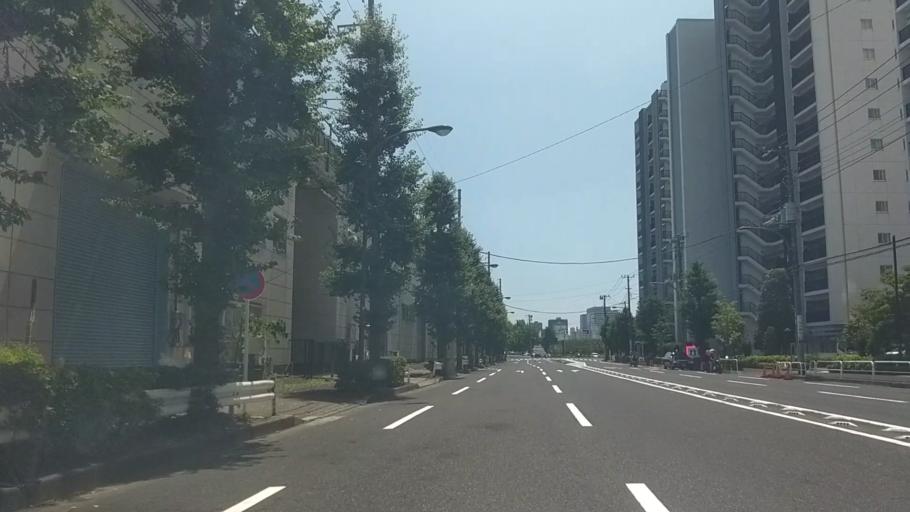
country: JP
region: Tokyo
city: Tokyo
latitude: 35.6235
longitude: 139.7541
